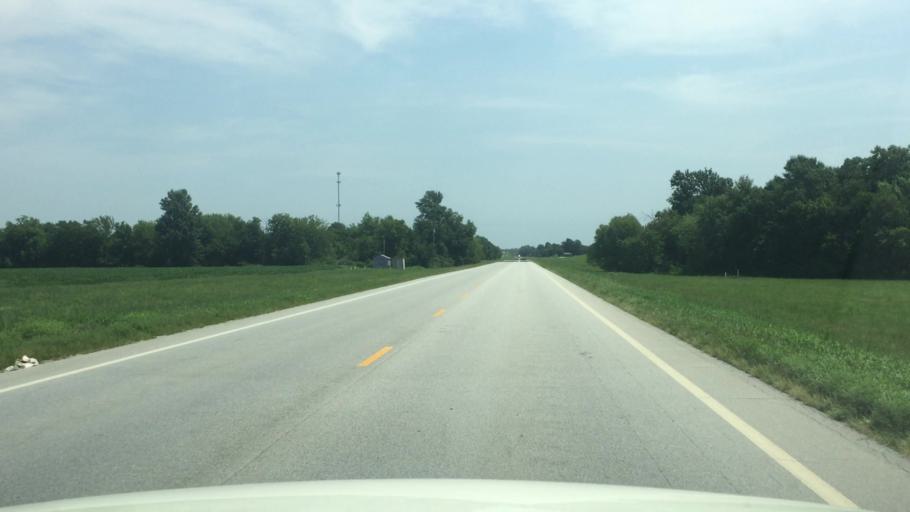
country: US
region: Kansas
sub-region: Cherokee County
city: Columbus
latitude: 37.1786
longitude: -94.8614
